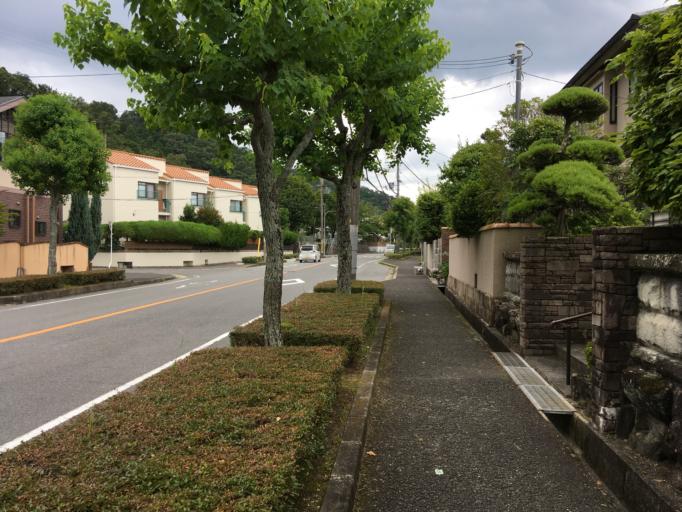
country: JP
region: Nara
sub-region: Ikoma-shi
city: Ikoma
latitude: 34.6795
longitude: 135.7182
